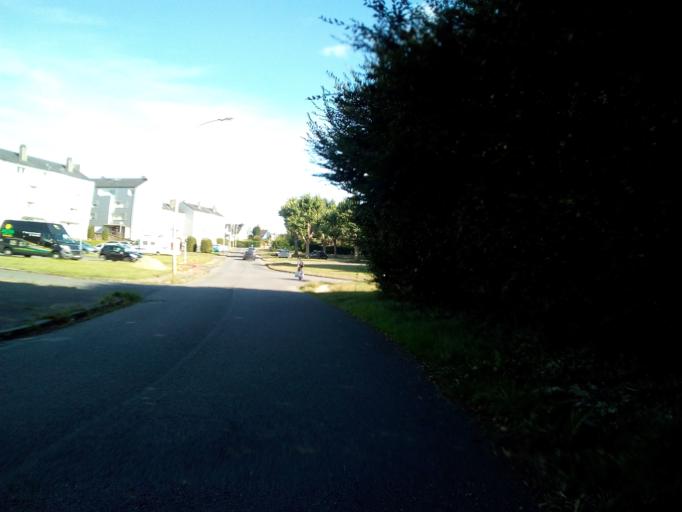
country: FR
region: Brittany
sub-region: Departement du Finistere
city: Landivisiau
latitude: 48.5069
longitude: -4.0776
